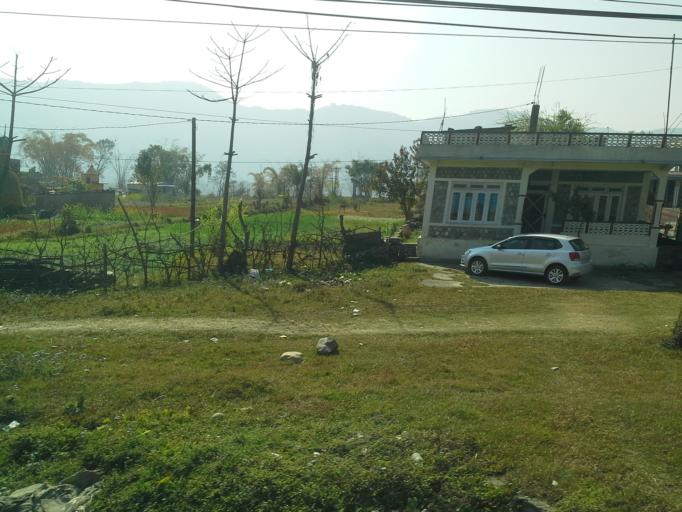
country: NP
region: Western Region
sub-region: Gandaki Zone
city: Pokhara
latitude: 28.1482
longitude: 84.0664
